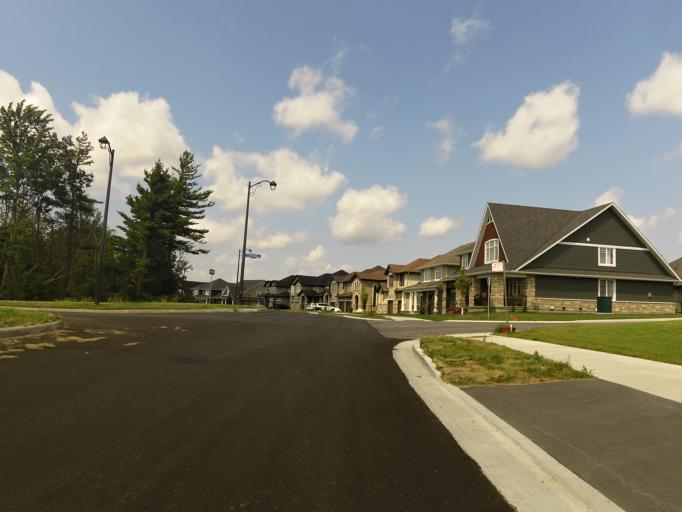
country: CA
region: Ontario
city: Bells Corners
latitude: 45.3172
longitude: -75.9366
